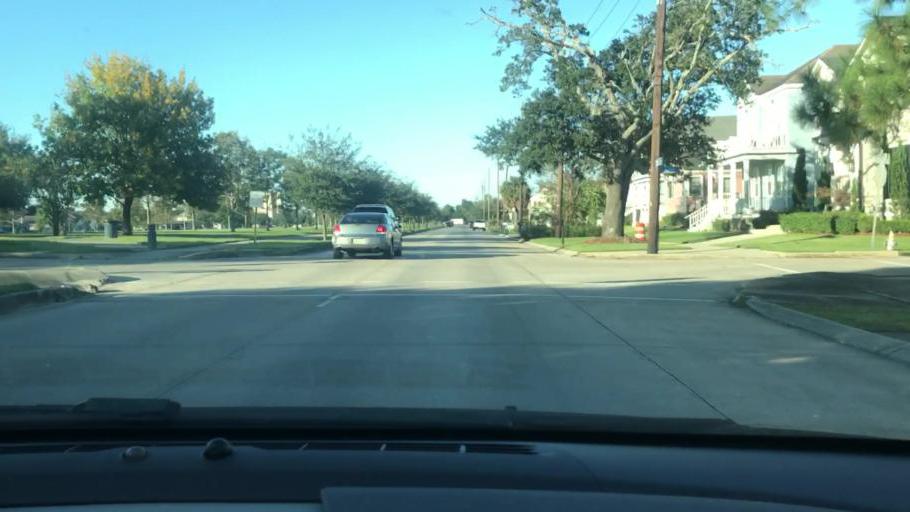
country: US
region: Louisiana
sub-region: Jefferson Parish
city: Metairie
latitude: 30.0089
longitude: -90.1144
